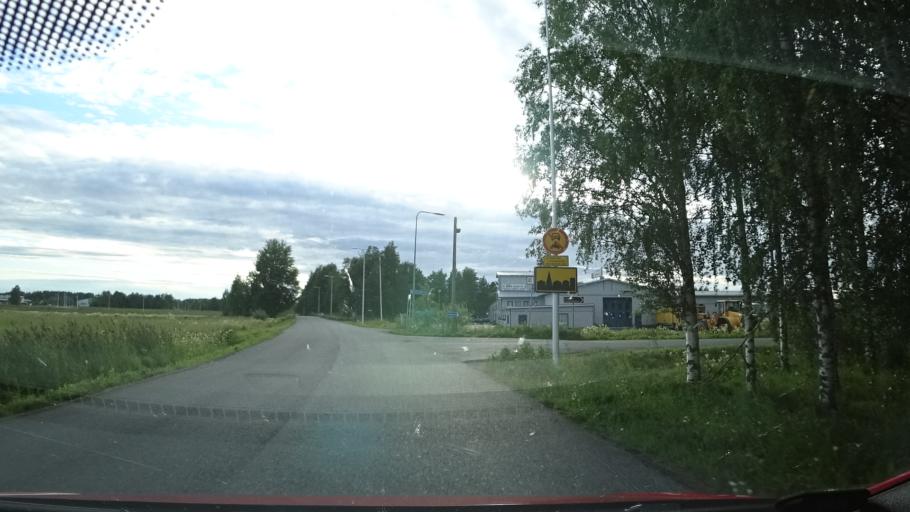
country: FI
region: Northern Ostrobothnia
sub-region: Oulu
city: Liminka
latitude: 64.8097
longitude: 25.4690
